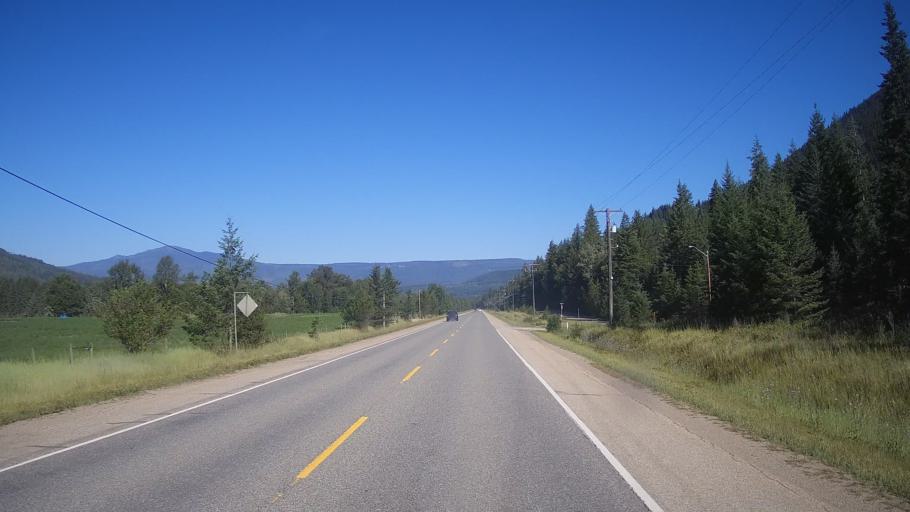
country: CA
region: British Columbia
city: Chase
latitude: 51.6213
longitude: -119.9410
